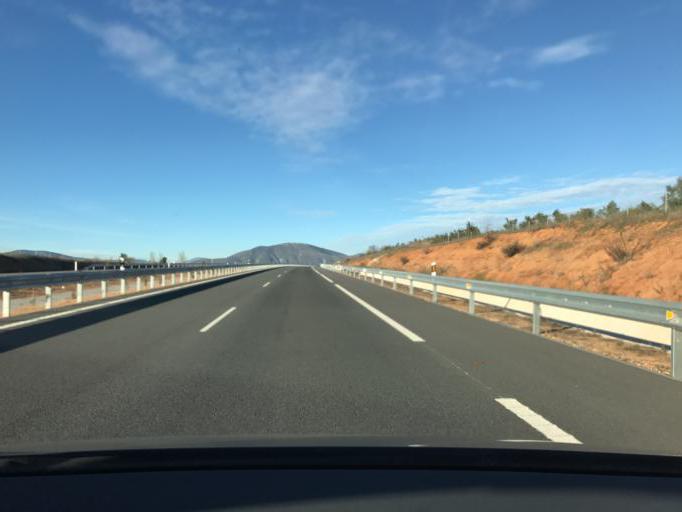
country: ES
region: Andalusia
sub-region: Provincia de Granada
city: Albolote
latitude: 37.2533
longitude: -3.6629
